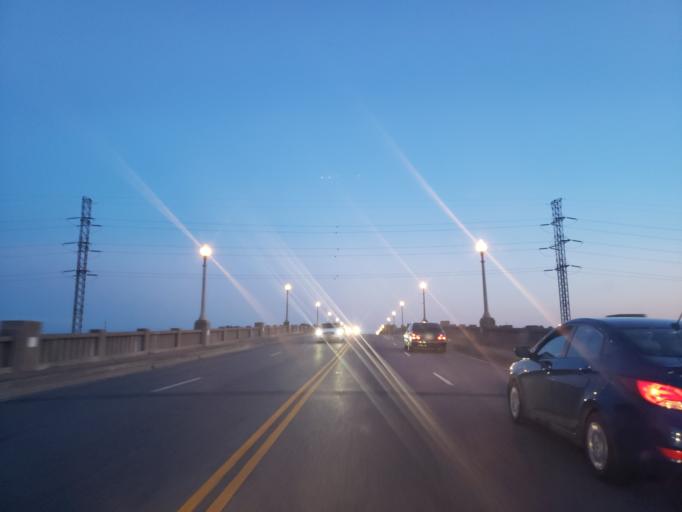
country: US
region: Texas
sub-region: Dallas County
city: Dallas
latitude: 32.7584
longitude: -96.7947
